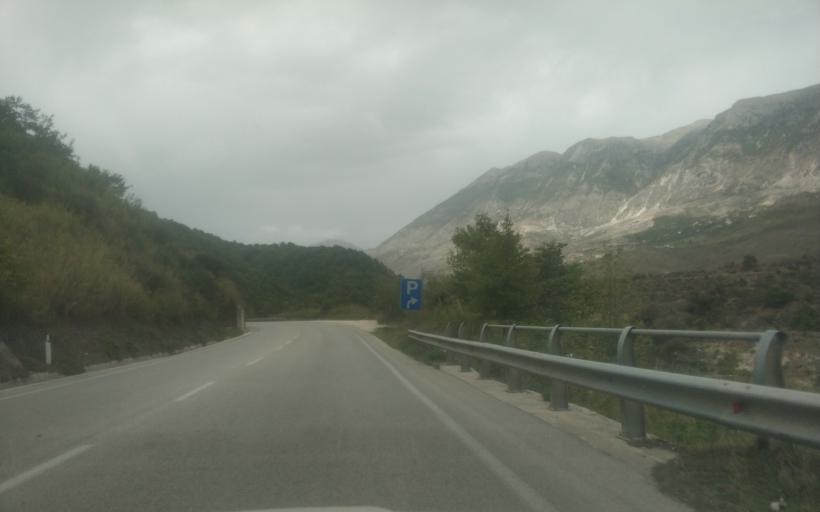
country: AL
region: Gjirokaster
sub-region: Rrethi i Gjirokastres
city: Picar
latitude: 40.2144
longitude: 20.0870
